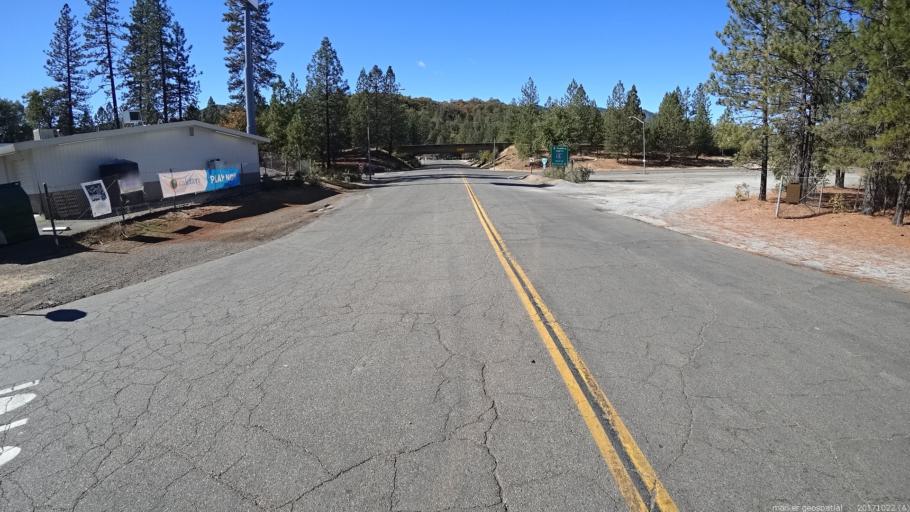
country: US
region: California
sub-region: Shasta County
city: Central Valley (historical)
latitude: 40.8925
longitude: -122.3818
